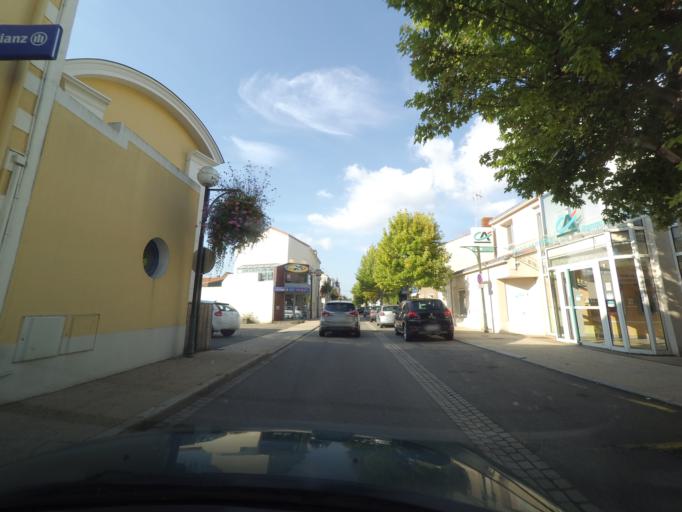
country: FR
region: Pays de la Loire
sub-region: Departement de la Loire-Atlantique
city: Saint-Philbert-de-Grand-Lieu
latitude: 47.0368
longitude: -1.6412
